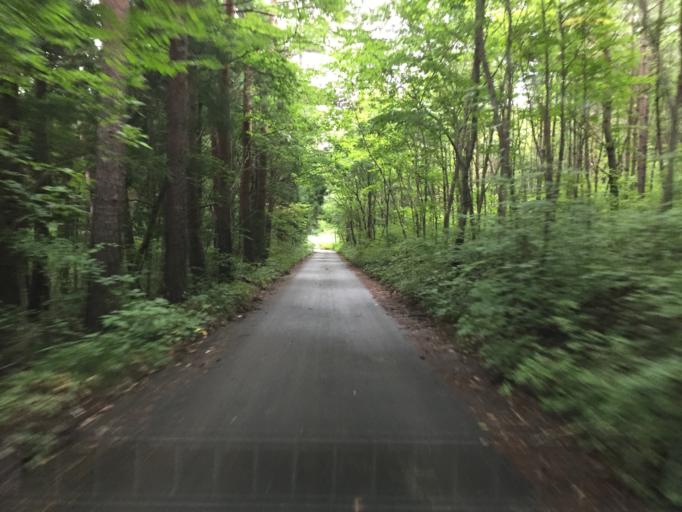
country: JP
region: Fukushima
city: Motomiya
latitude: 37.5658
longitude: 140.3110
